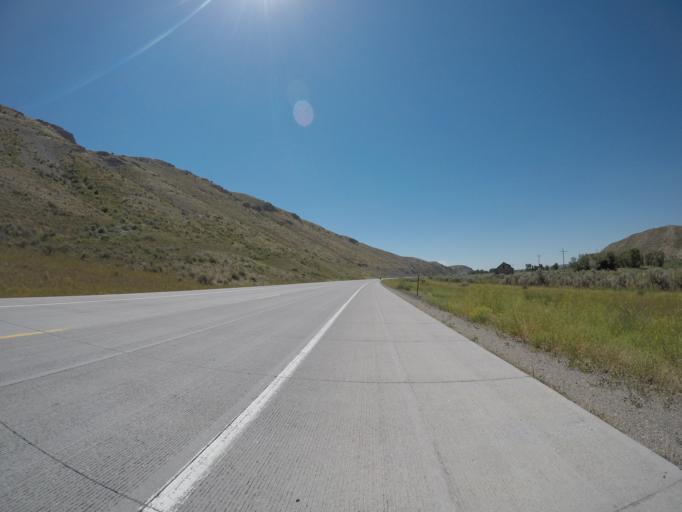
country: US
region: Idaho
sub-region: Bear Lake County
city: Montpelier
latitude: 42.1396
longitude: -110.9716
